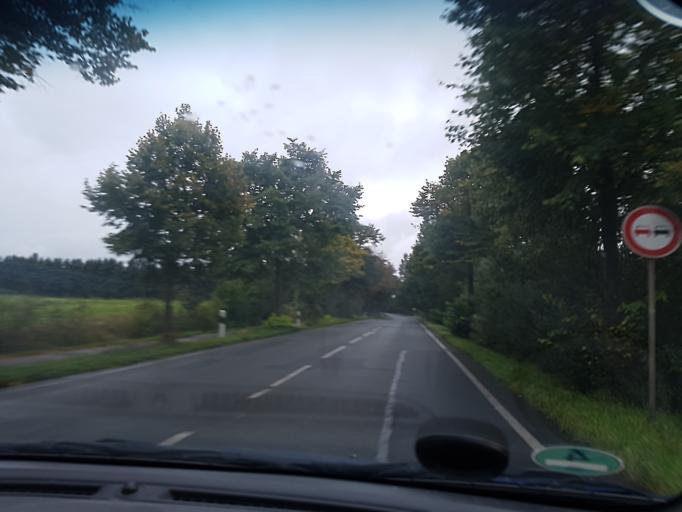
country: DE
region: Lower Saxony
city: Garbsen-Mitte
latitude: 52.4355
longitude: 9.6437
